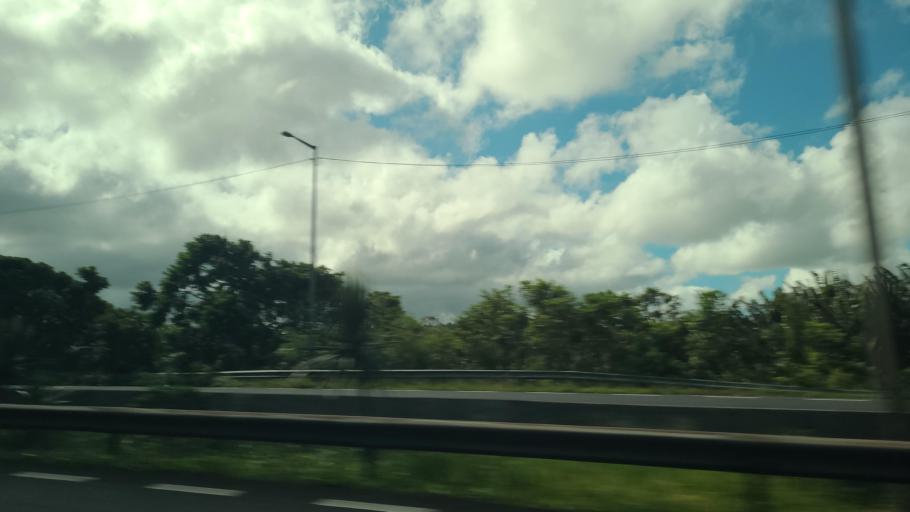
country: MU
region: Plaines Wilhems
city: Midlands
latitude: -20.3309
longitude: 57.5555
